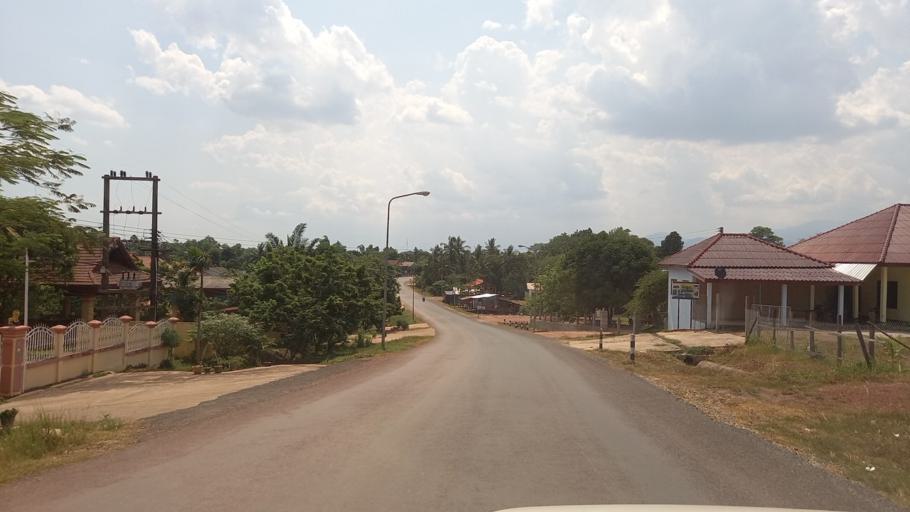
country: LA
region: Bolikhamxai
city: Muang Pakxan
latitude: 18.4170
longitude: 103.6403
